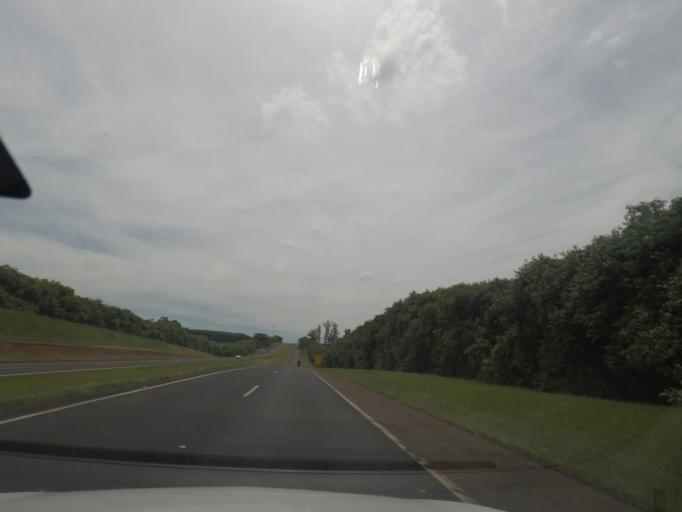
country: BR
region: Sao Paulo
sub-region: Bebedouro
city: Bebedouro
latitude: -21.0002
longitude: -48.4305
